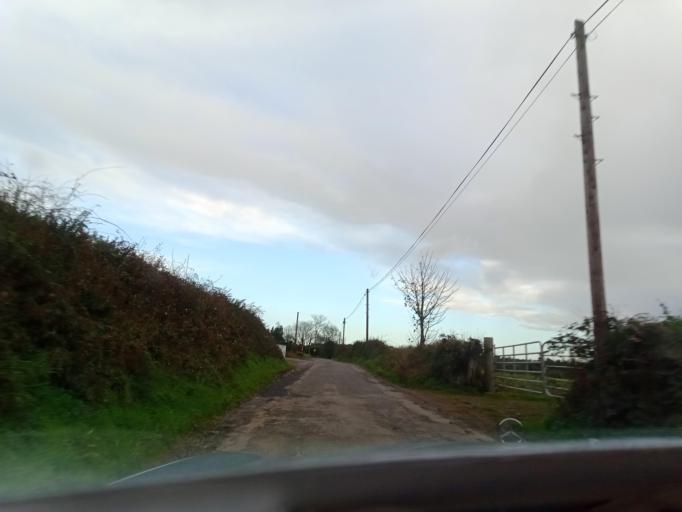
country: IE
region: Munster
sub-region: Waterford
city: Waterford
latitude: 52.3309
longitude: -7.0378
